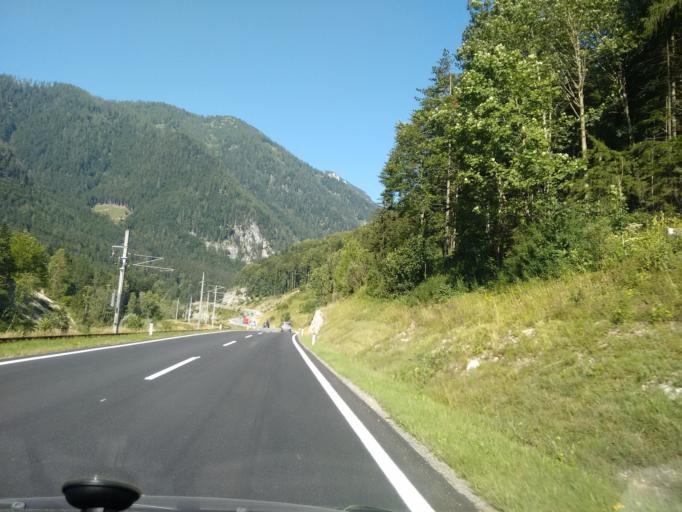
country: AT
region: Styria
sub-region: Politischer Bezirk Liezen
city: Bad Aussee
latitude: 47.5763
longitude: 13.8193
